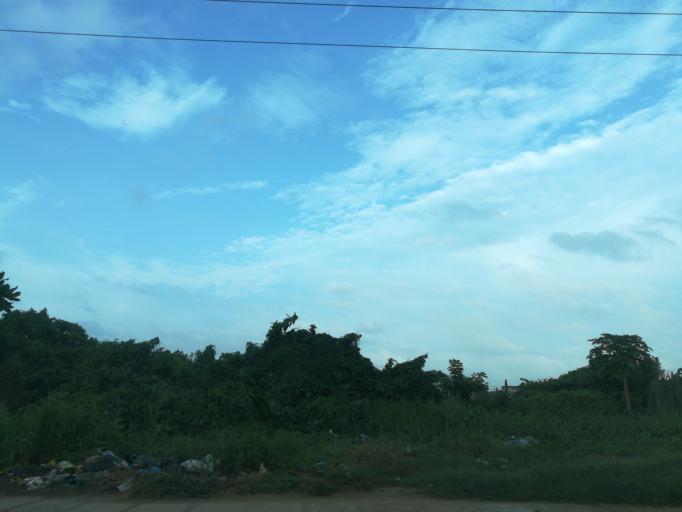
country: NG
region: Lagos
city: Ebute Ikorodu
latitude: 6.6070
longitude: 3.4848
